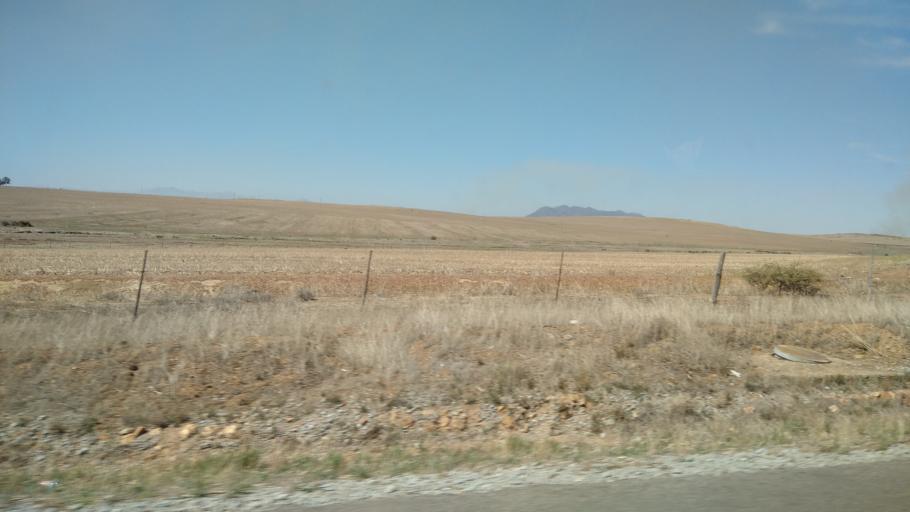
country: ZA
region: Western Cape
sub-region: West Coast District Municipality
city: Malmesbury
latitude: -33.3494
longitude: 18.6409
